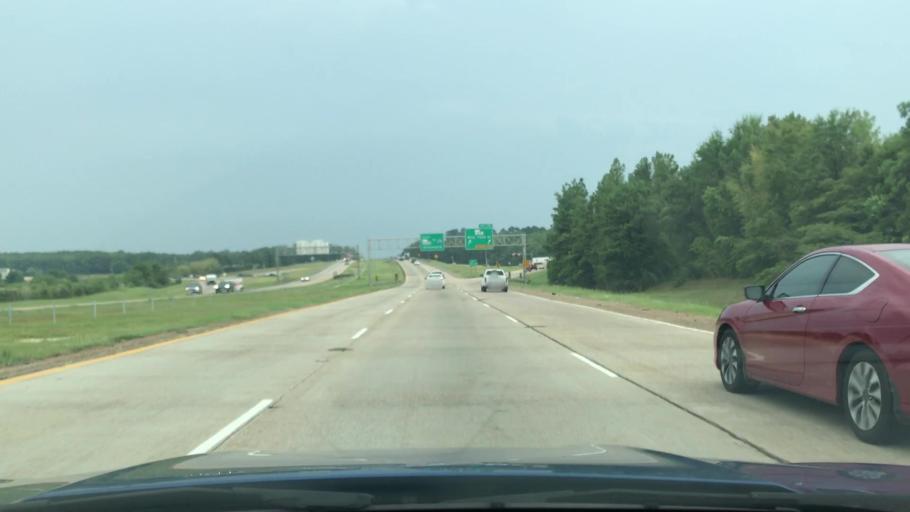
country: US
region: Louisiana
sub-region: Caddo Parish
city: Shreveport
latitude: 32.4465
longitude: -93.8429
